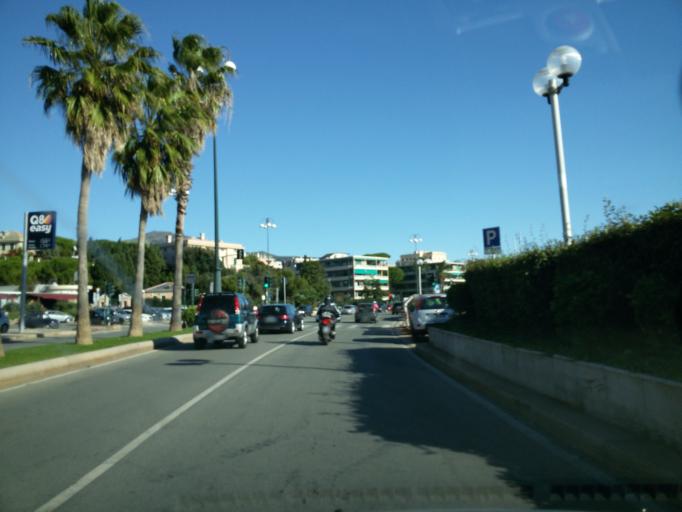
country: IT
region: Liguria
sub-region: Provincia di Genova
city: San Teodoro
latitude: 44.3914
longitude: 8.9665
